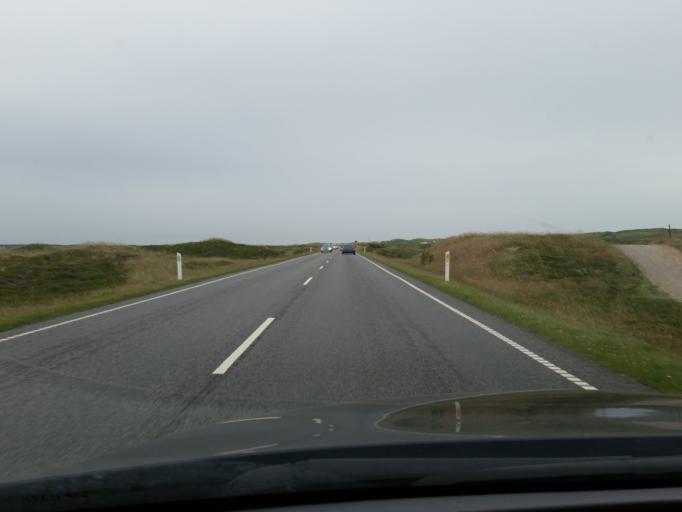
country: DK
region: Central Jutland
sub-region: Ringkobing-Skjern Kommune
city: Hvide Sande
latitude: 55.8355
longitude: 8.1727
